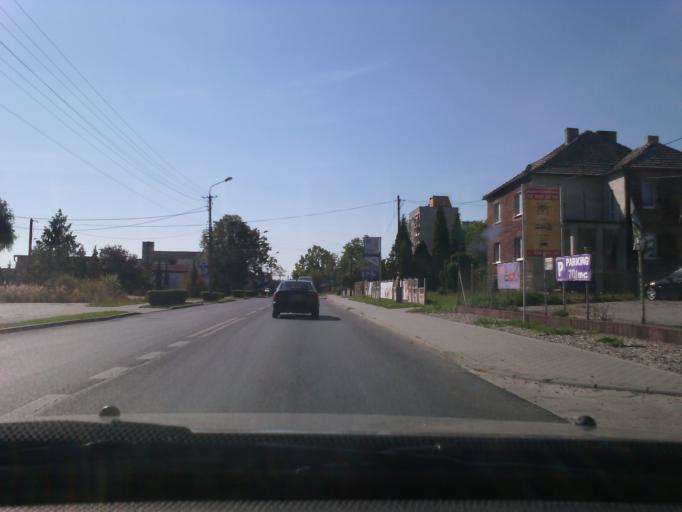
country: PL
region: Silesian Voivodeship
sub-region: Rybnik
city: Rybnik
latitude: 50.0881
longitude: 18.5314
